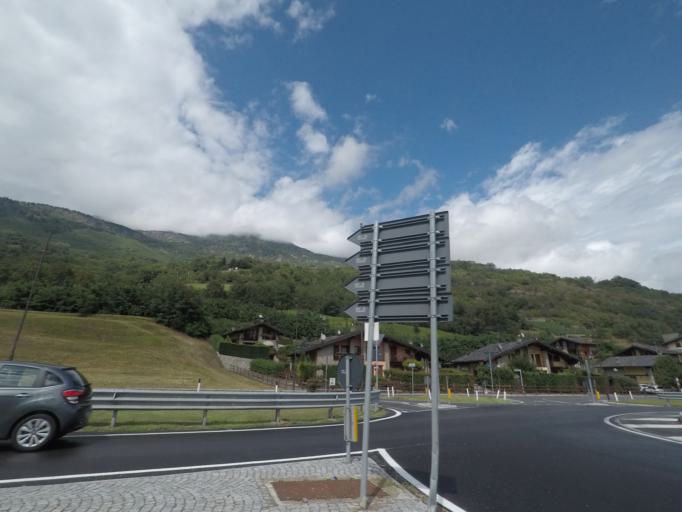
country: IT
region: Aosta Valley
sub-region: Valle d'Aosta
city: Quart
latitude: 45.7416
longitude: 7.4083
